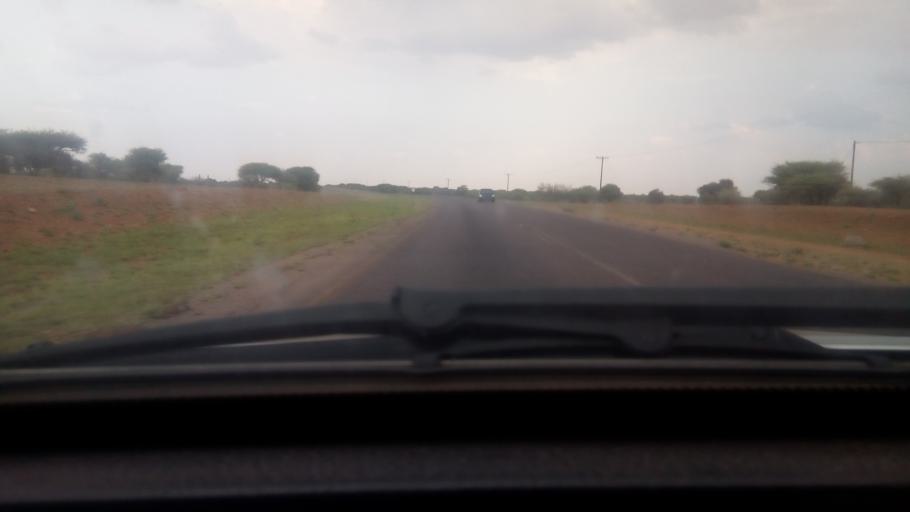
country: BW
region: Kweneng
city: Metsemotlhaba
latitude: -24.4665
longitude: 25.6742
